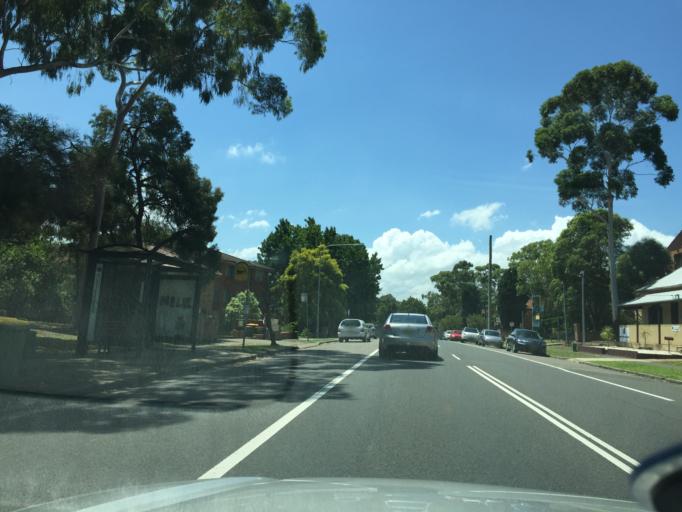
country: AU
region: New South Wales
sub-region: Parramatta
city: City of Parramatta
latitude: -33.8027
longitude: 151.0031
